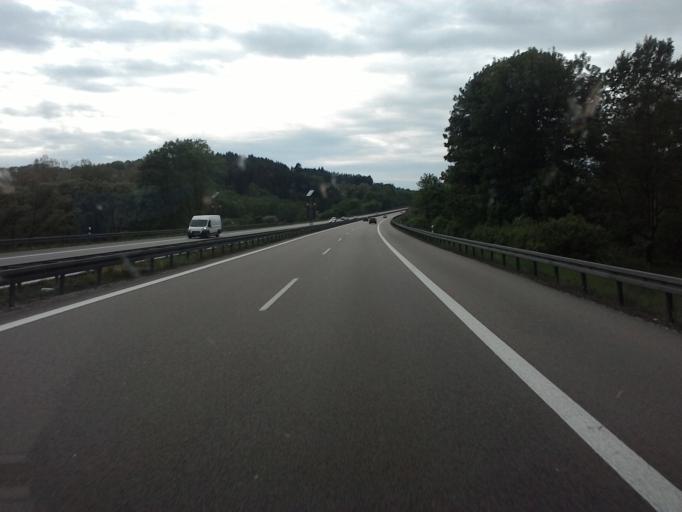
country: DE
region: Bavaria
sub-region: Upper Palatinate
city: Velburg
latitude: 49.2467
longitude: 11.6234
